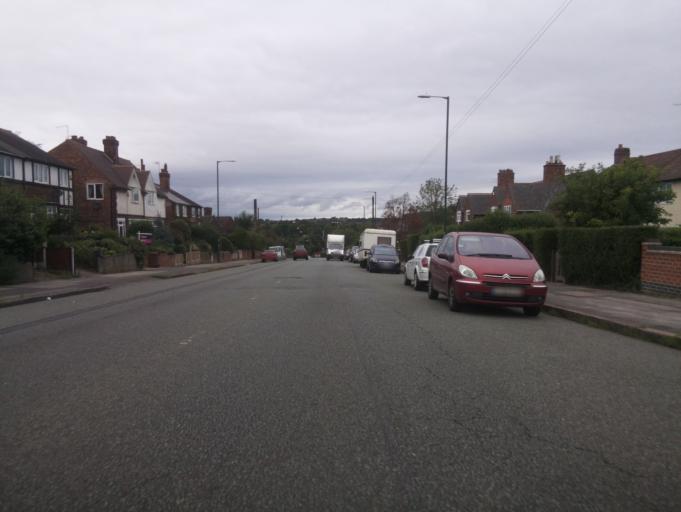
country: GB
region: England
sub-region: Nottinghamshire
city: Arnold
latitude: 52.9859
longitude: -1.1478
